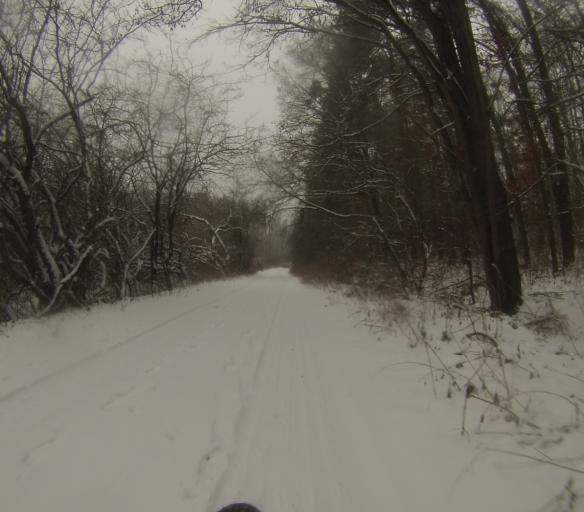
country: CZ
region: South Moravian
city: Orechov
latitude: 49.1308
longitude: 16.5387
